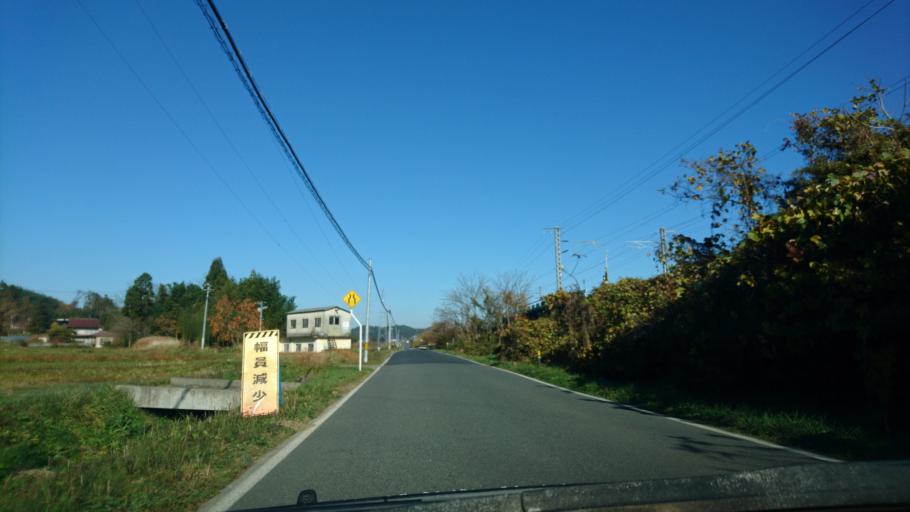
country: JP
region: Iwate
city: Mizusawa
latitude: 39.0274
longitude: 141.1286
